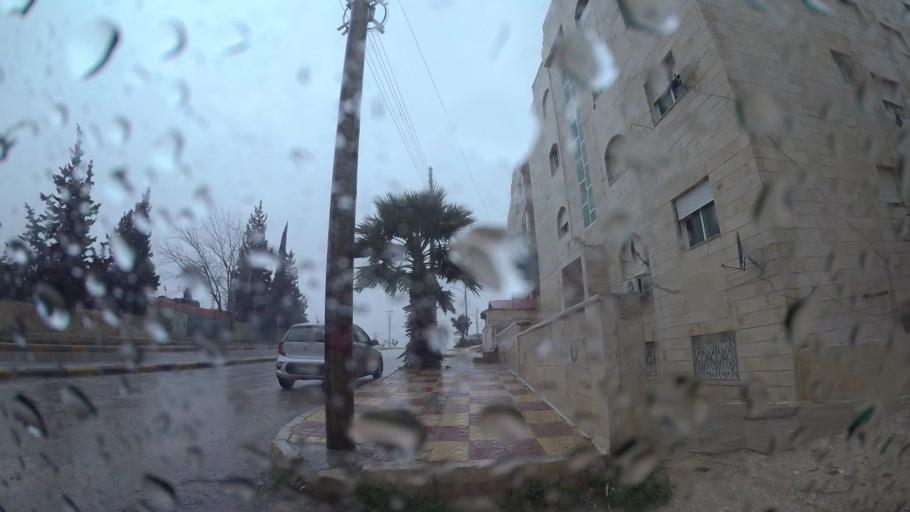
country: JO
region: Amman
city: Al Jubayhah
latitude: 32.0473
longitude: 35.8740
